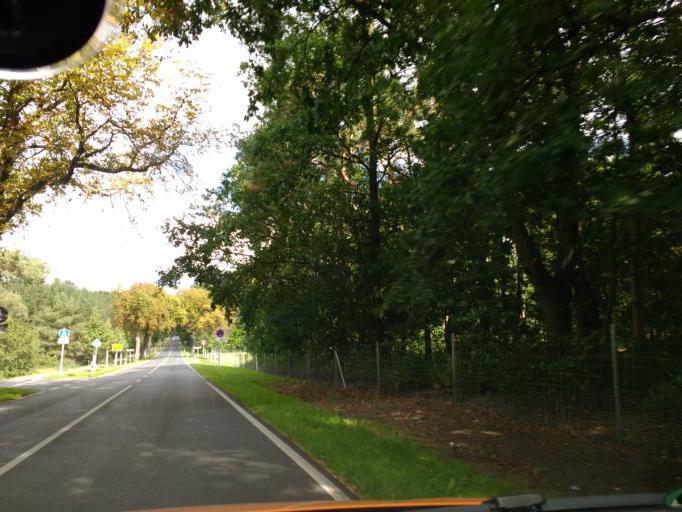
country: DE
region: Brandenburg
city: Wandlitz
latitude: 52.8032
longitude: 13.4863
